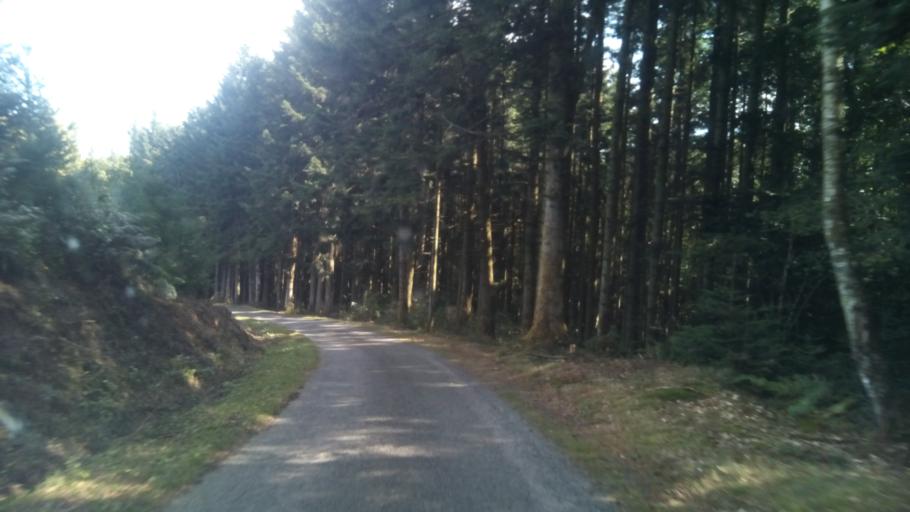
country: FR
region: Rhone-Alpes
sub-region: Departement du Rhone
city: Beaujeu
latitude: 46.2031
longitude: 4.5134
